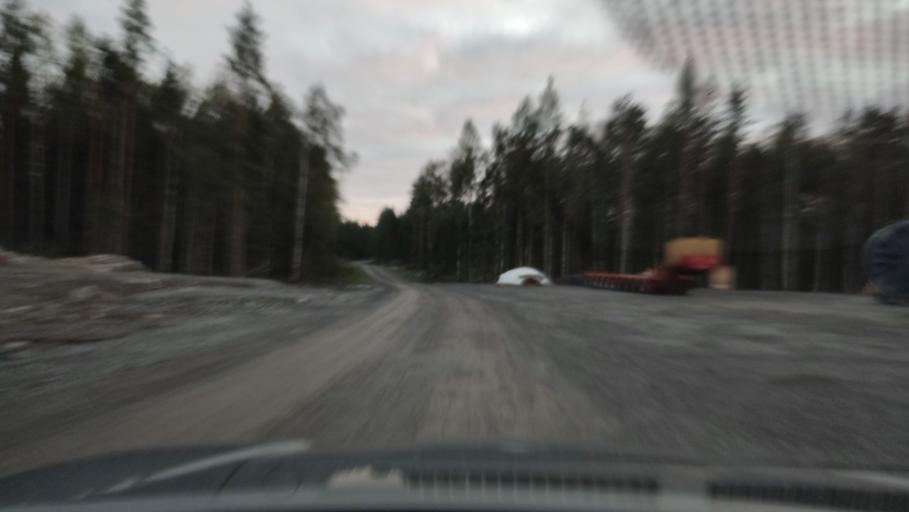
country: FI
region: Ostrobothnia
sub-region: Sydosterbotten
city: Kristinestad
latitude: 62.1907
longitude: 21.5411
